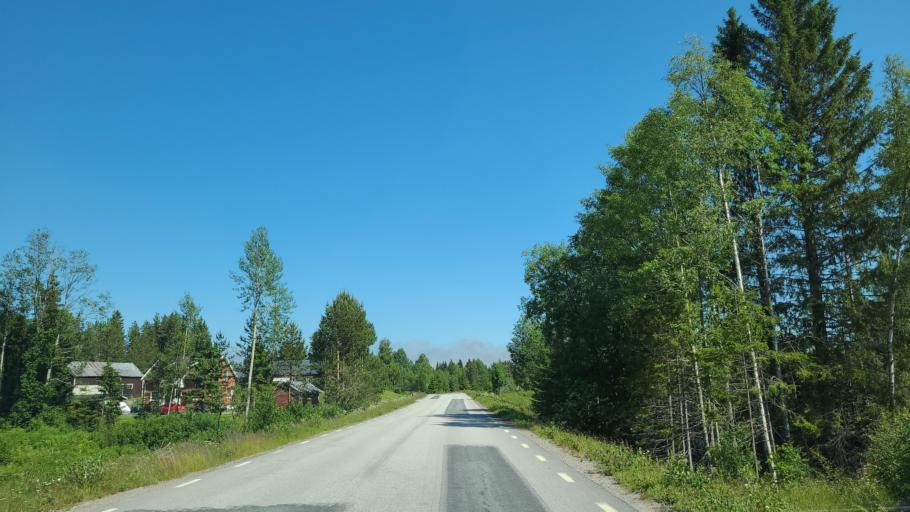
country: SE
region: Vaesternorrland
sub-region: OErnskoeldsviks Kommun
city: Husum
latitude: 63.3897
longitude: 19.2093
